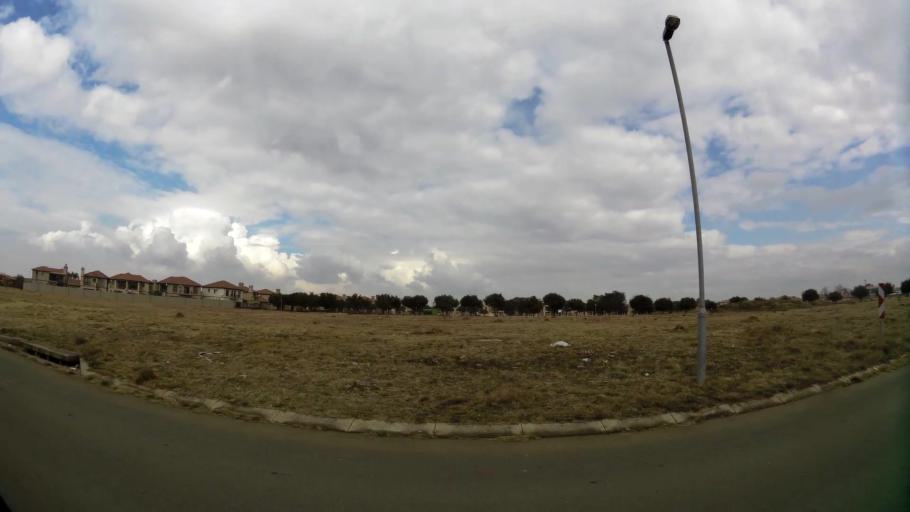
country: ZA
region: Gauteng
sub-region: Sedibeng District Municipality
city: Vanderbijlpark
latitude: -26.7243
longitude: 27.8673
